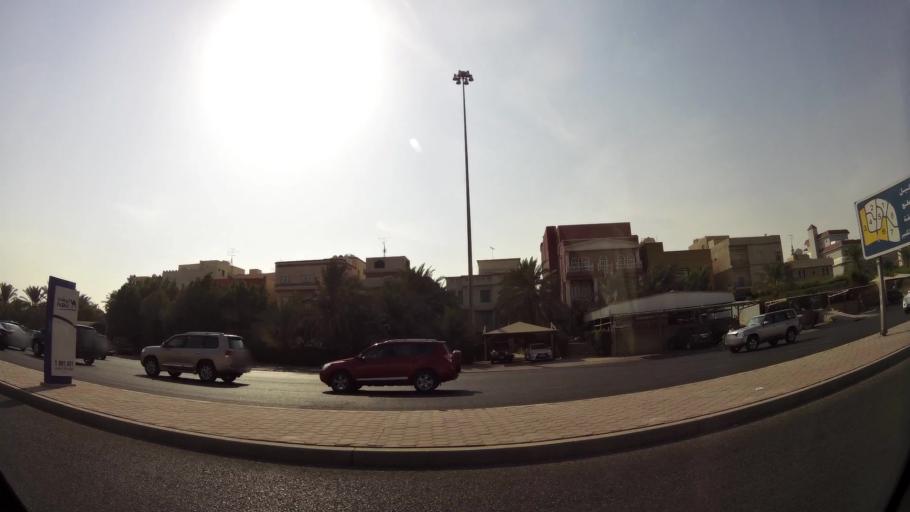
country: KW
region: Mubarak al Kabir
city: Mubarak al Kabir
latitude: 29.1823
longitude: 48.0820
